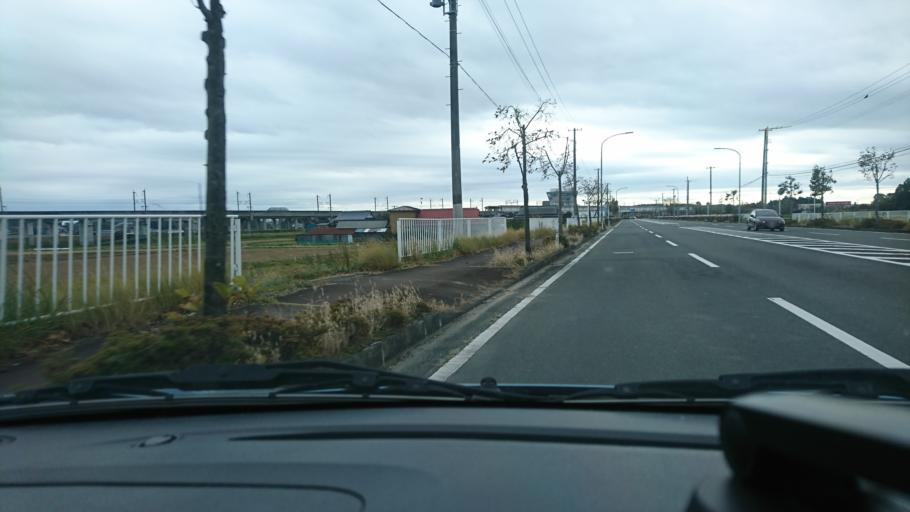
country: JP
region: Iwate
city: Ichinoseki
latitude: 38.7542
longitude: 141.0715
